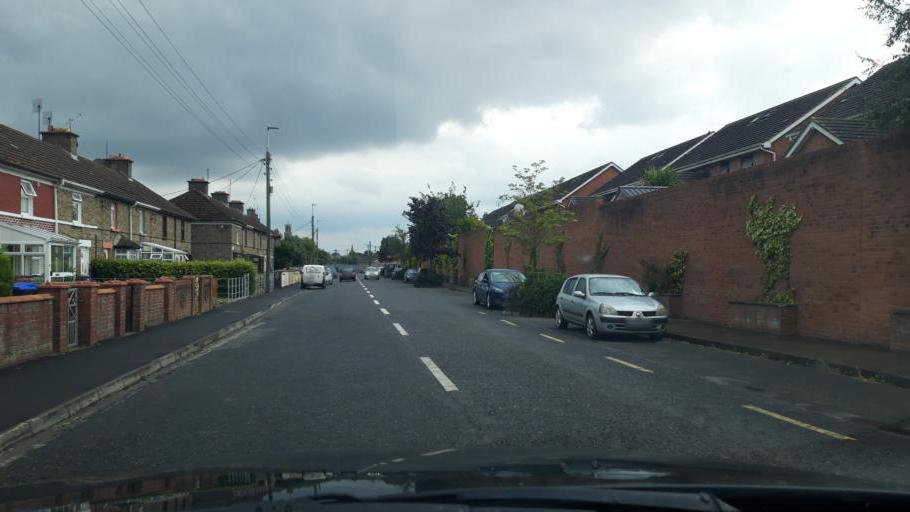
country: IE
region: Leinster
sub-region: Kildare
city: Athy
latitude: 52.9986
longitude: -6.9875
